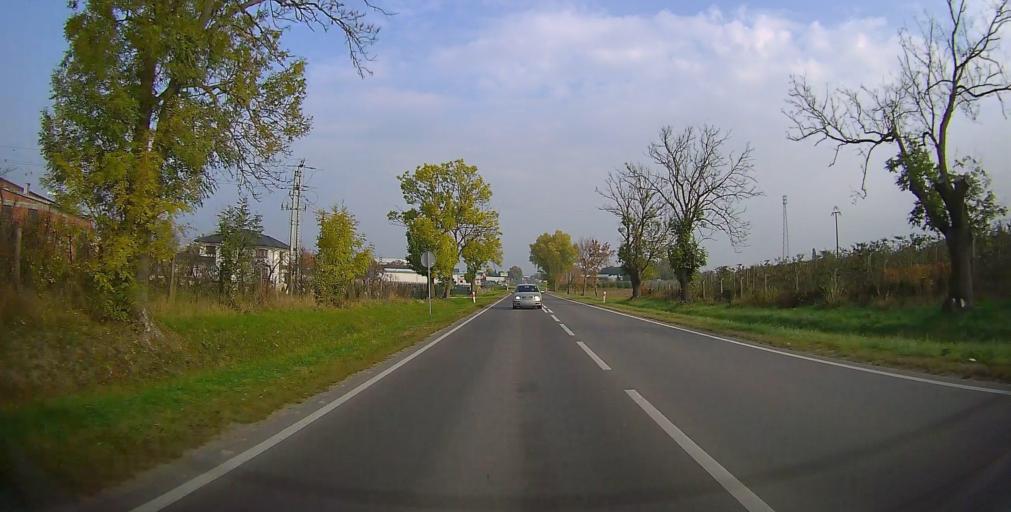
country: PL
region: Masovian Voivodeship
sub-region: Powiat grojecki
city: Mogielnica
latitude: 51.7336
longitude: 20.7541
